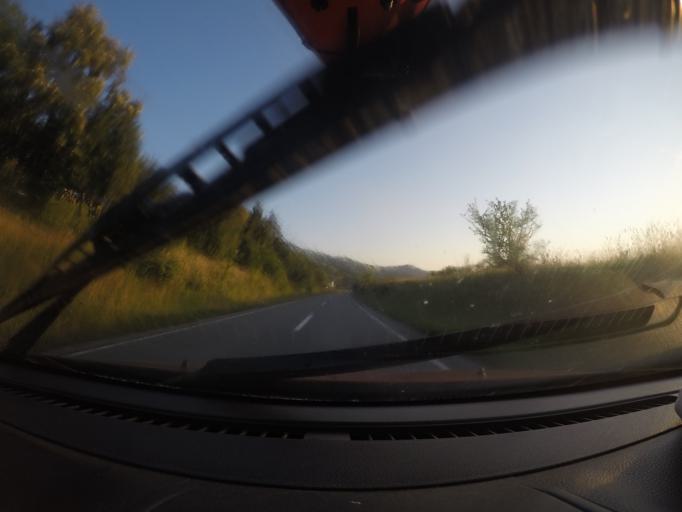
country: RO
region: Mehedinti
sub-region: Municipiul Orsova
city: Orsova
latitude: 44.6809
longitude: 22.4047
